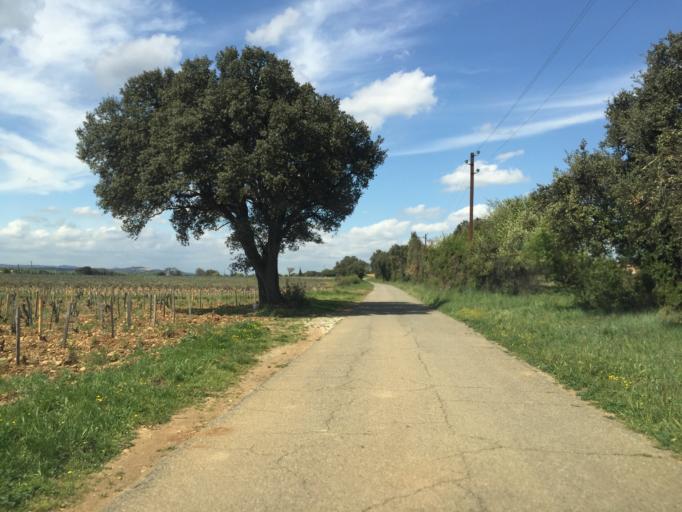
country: FR
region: Provence-Alpes-Cote d'Azur
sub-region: Departement du Vaucluse
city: Chateauneuf-du-Pape
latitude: 44.0461
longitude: 4.8412
